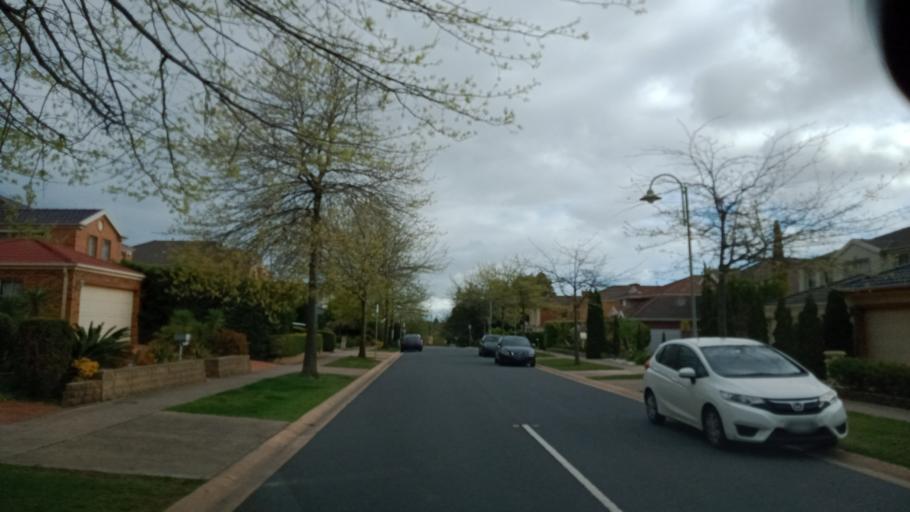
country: AU
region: Victoria
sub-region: Monash
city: Notting Hill
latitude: -37.8784
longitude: 145.1531
